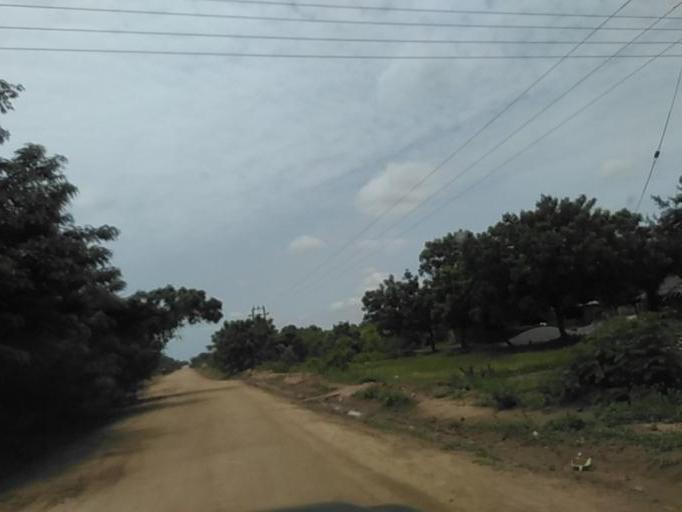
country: GH
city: Akropong
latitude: 6.0521
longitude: 0.2948
